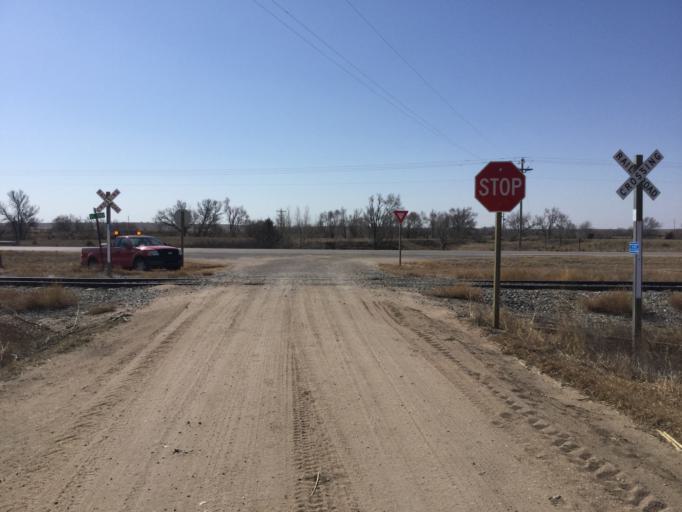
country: US
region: Kansas
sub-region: Rush County
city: La Crosse
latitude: 38.4713
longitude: -99.4010
